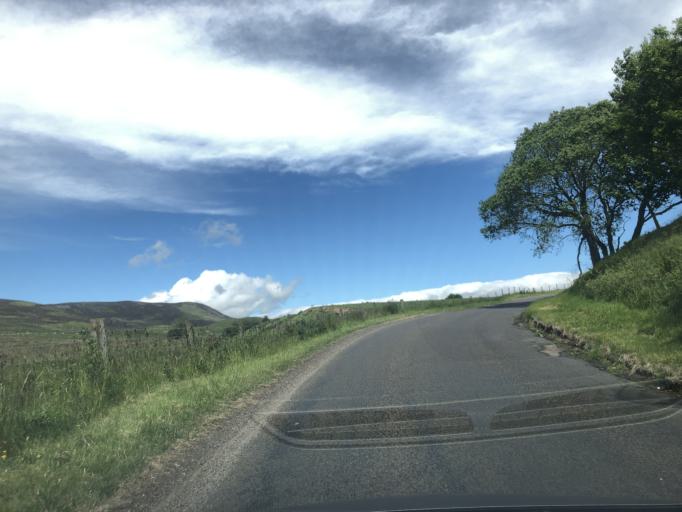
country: GB
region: Scotland
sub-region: Angus
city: Kirriemuir
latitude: 56.7552
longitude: -3.0166
